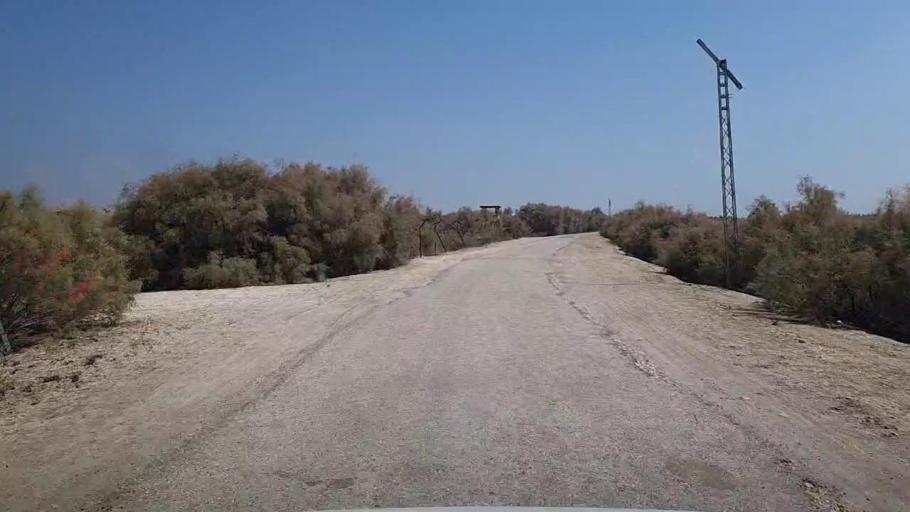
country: PK
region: Sindh
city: Kandhkot
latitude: 28.3011
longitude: 69.3510
